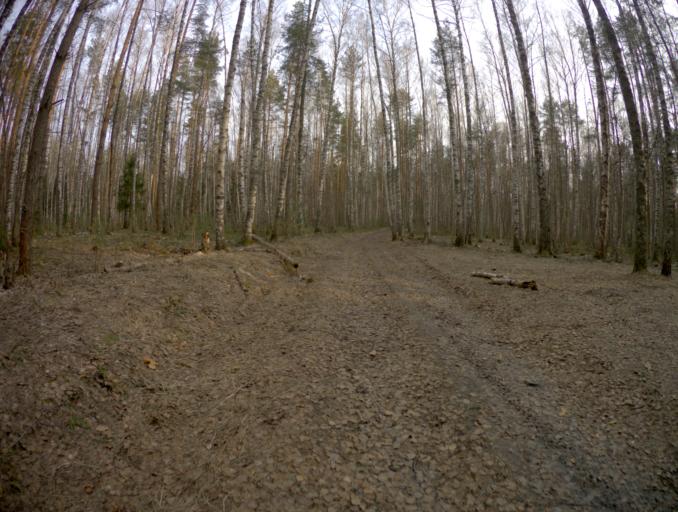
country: RU
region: Vladimir
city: Kommunar
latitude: 56.0766
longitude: 40.4398
